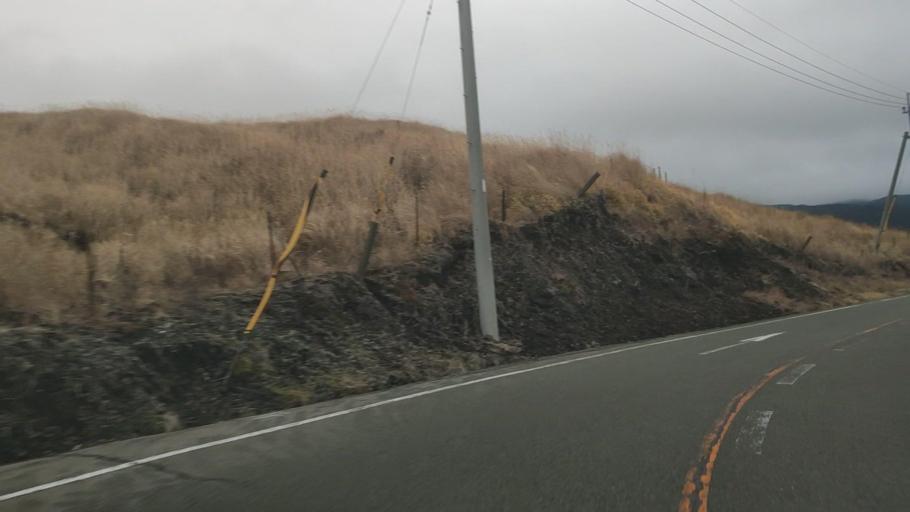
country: JP
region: Kumamoto
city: Aso
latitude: 32.9050
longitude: 131.0365
